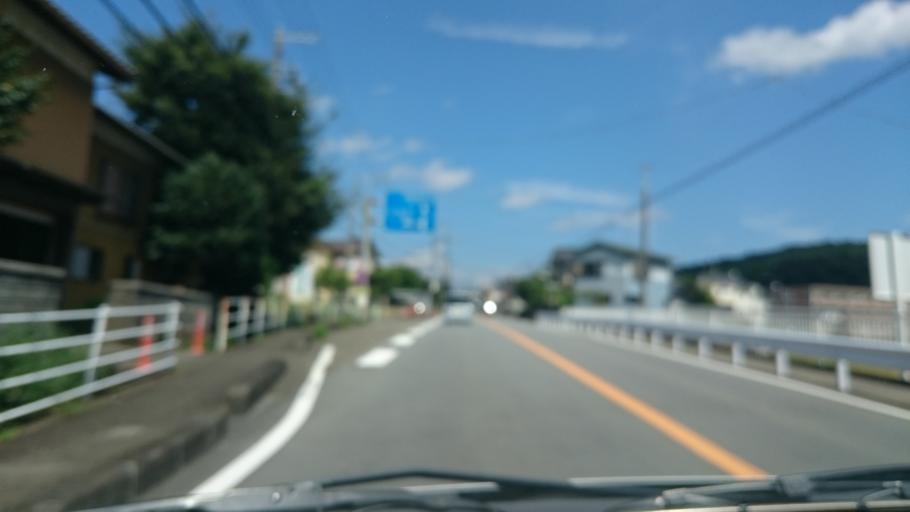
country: JP
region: Shizuoka
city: Gotemba
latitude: 35.2434
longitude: 138.9222
